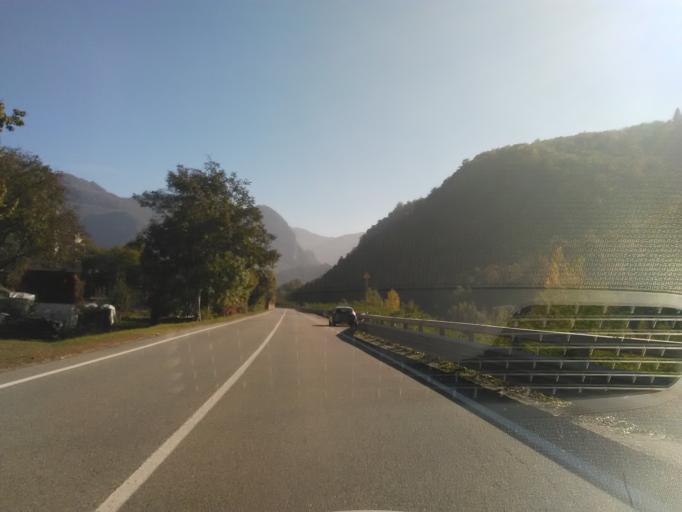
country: IT
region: Piedmont
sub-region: Provincia di Vercelli
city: Varallo
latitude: 45.8140
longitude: 8.2454
